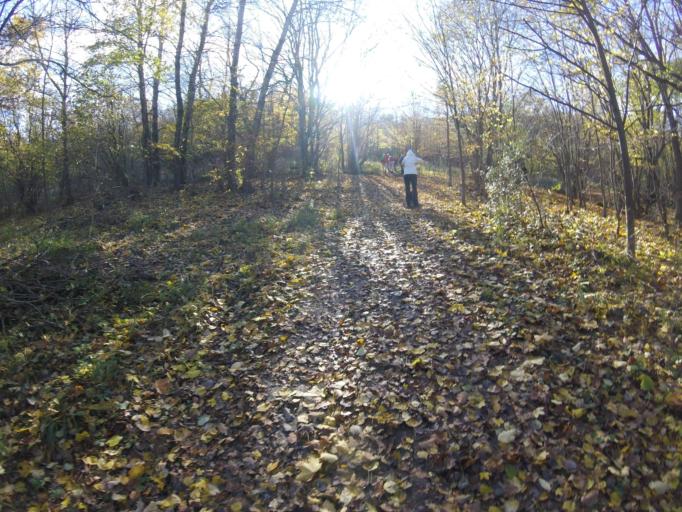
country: HU
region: Borsod-Abauj-Zemplen
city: Tolcsva
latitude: 48.3775
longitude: 21.3968
